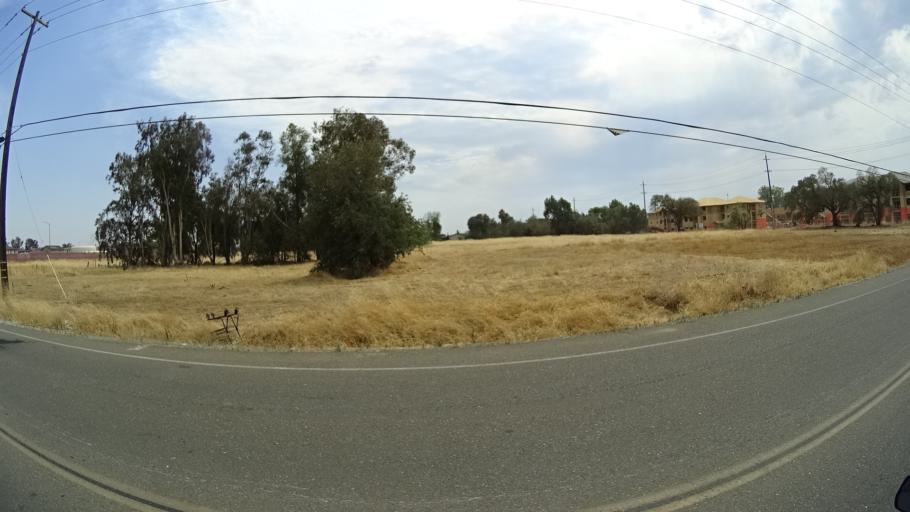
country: US
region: California
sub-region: Sacramento County
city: Laguna
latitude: 38.3908
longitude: -121.4163
